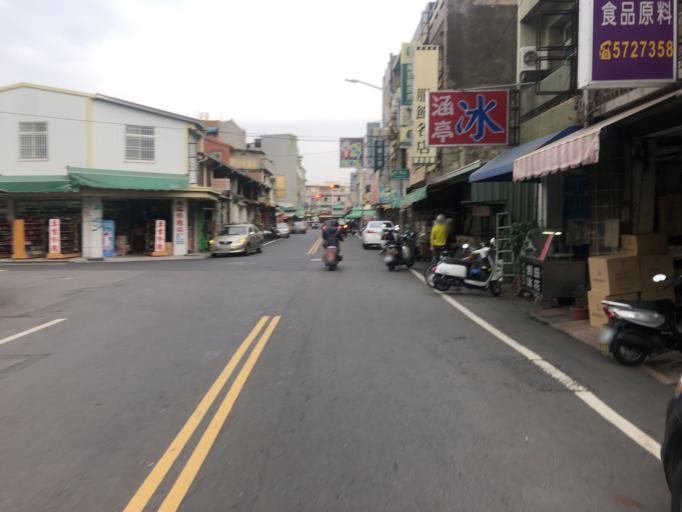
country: TW
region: Taiwan
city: Xinying
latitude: 23.1845
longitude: 120.2478
